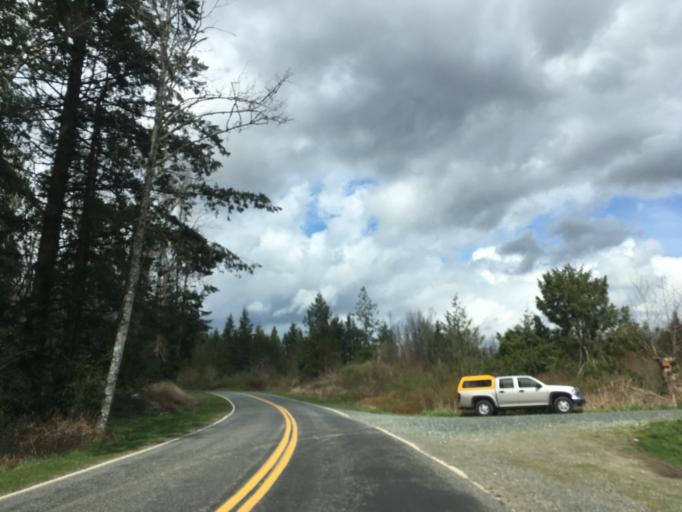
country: US
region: Washington
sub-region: Whatcom County
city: Sudden Valley
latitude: 48.7636
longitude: -122.3454
